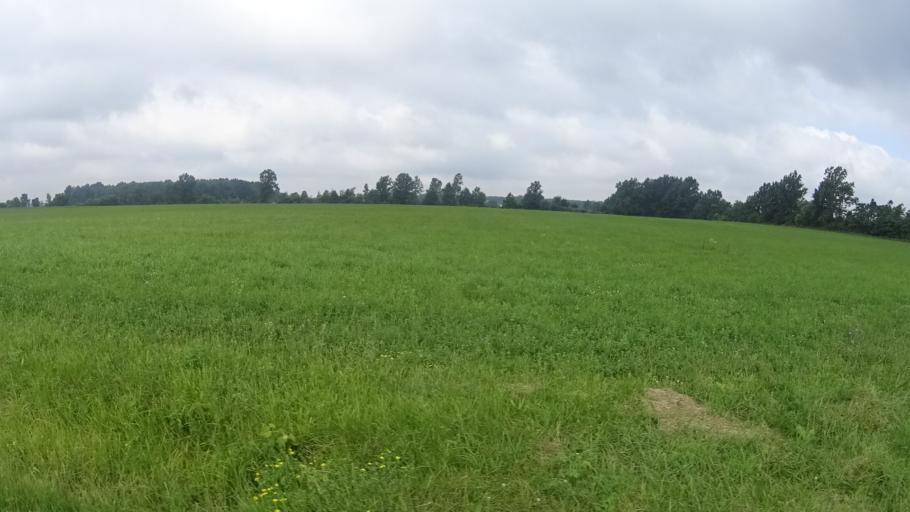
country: US
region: Ohio
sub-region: Huron County
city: Wakeman
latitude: 41.2894
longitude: -82.4809
